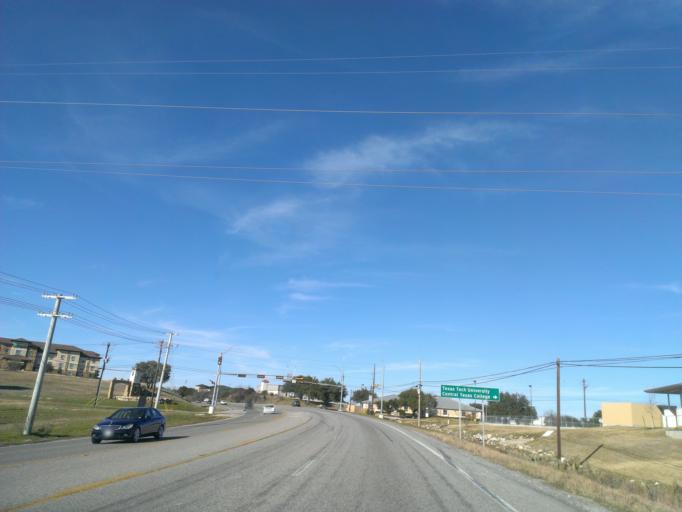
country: US
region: Texas
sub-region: Burnet County
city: Meadowlakes
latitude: 30.5547
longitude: -98.2738
